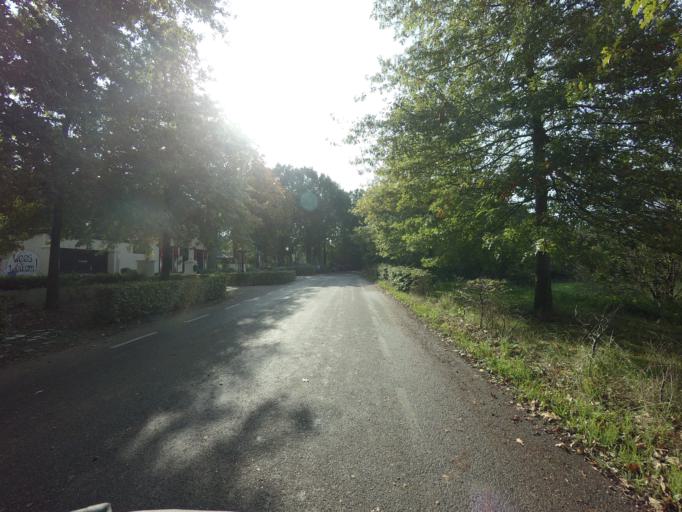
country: NL
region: North Brabant
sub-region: Gemeente Made en Drimmelen
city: Made
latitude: 51.6468
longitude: 4.8082
